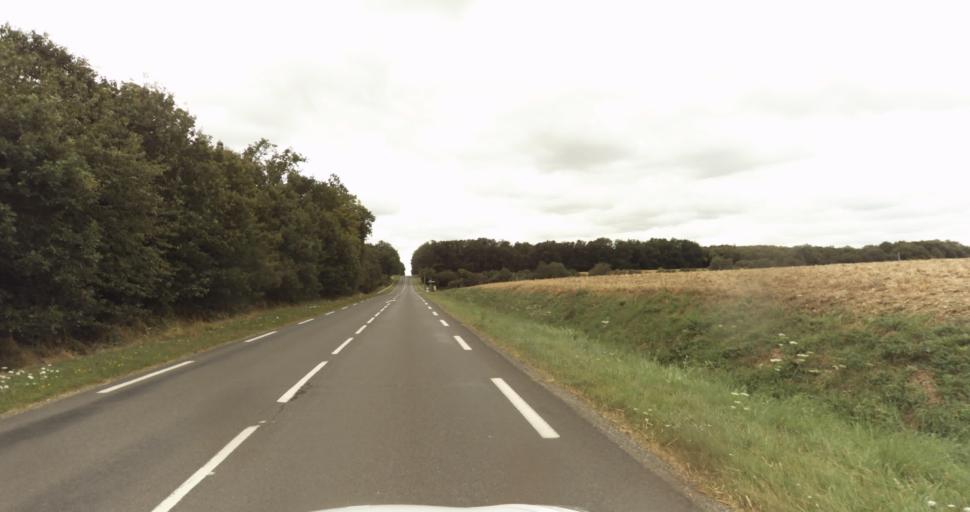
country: FR
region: Haute-Normandie
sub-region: Departement de l'Eure
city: La Madeleine-de-Nonancourt
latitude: 48.8143
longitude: 1.1874
